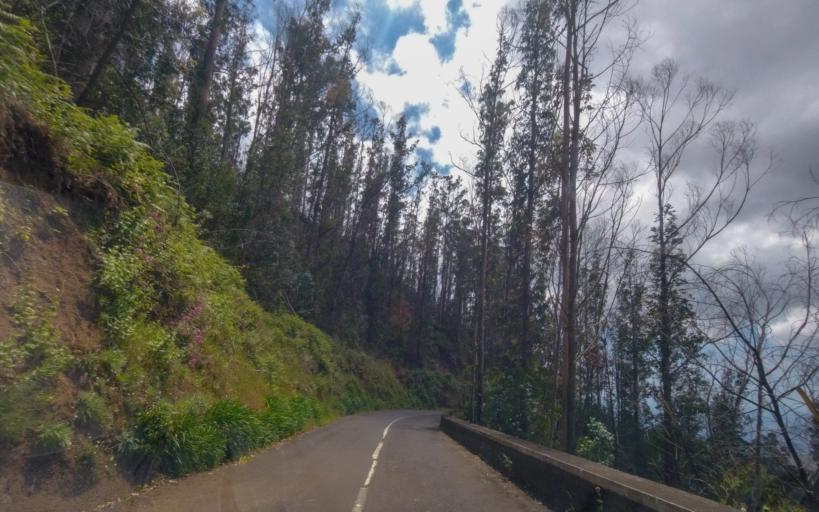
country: PT
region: Madeira
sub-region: Funchal
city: Nossa Senhora do Monte
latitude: 32.6767
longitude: -16.8833
